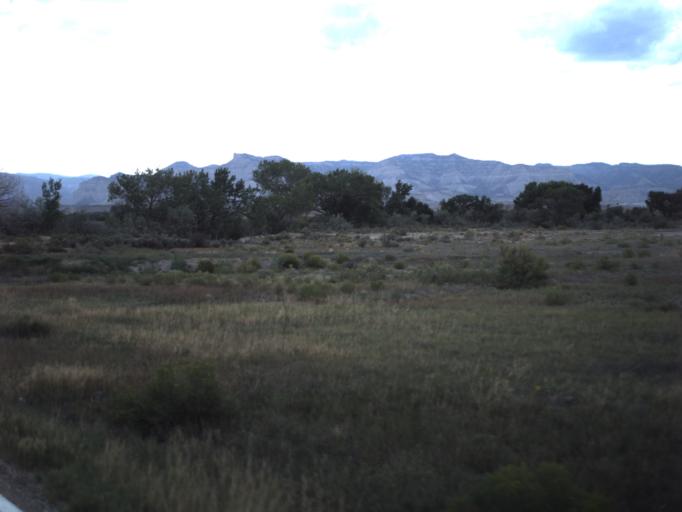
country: US
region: Utah
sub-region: Emery County
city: Huntington
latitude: 39.3450
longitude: -110.9248
